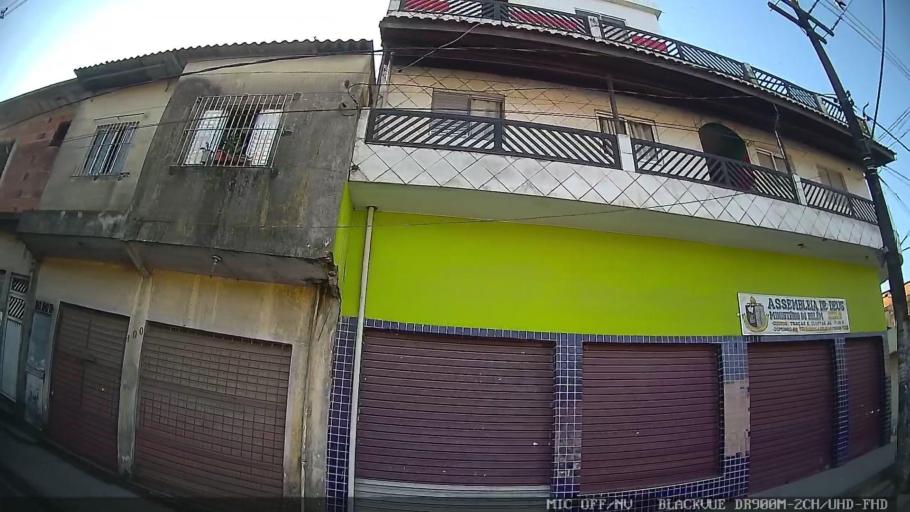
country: BR
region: Sao Paulo
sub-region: Guaruja
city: Guaruja
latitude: -23.9625
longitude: -46.2452
